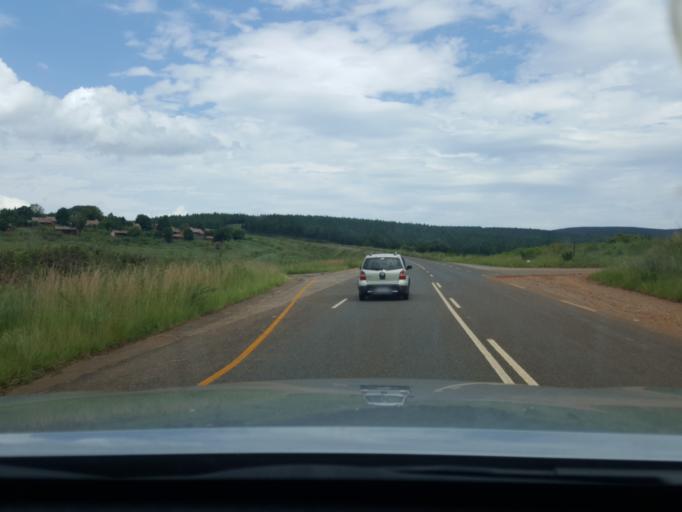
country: ZA
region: Mpumalanga
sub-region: Ehlanzeni District
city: Graksop
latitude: -25.1265
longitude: 30.8075
